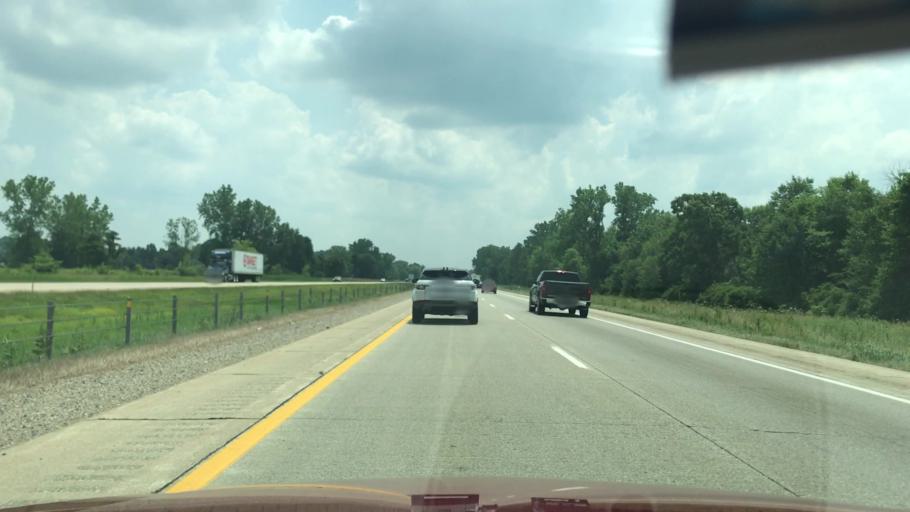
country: US
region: Michigan
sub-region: Allegan County
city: Plainwell
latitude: 42.4259
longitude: -85.6608
